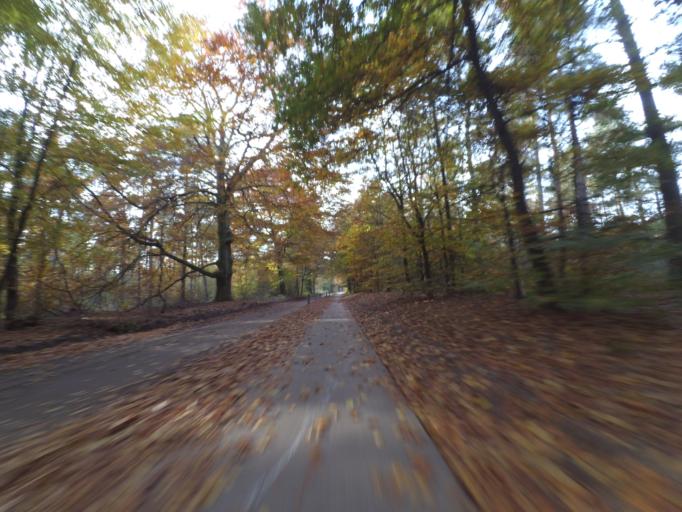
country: NL
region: Gelderland
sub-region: Gemeente Renkum
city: Heelsum
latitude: 52.0127
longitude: 5.7505
